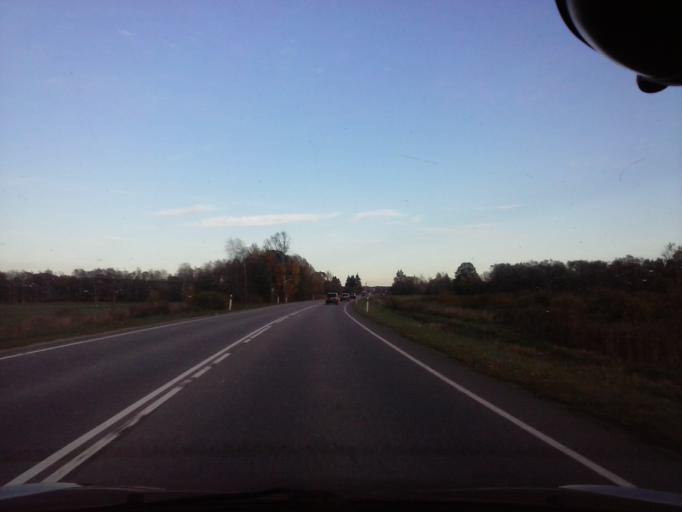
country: EE
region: Laeaene
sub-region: Ridala Parish
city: Uuemoisa
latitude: 58.9733
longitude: 23.8541
